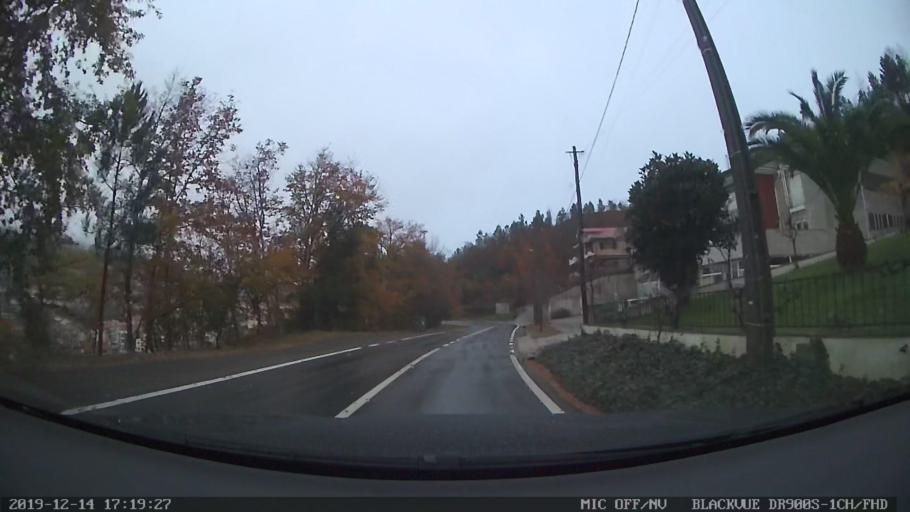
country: PT
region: Vila Real
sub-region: Vila Pouca de Aguiar
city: Vila Pouca de Aguiar
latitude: 41.4954
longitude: -7.6408
